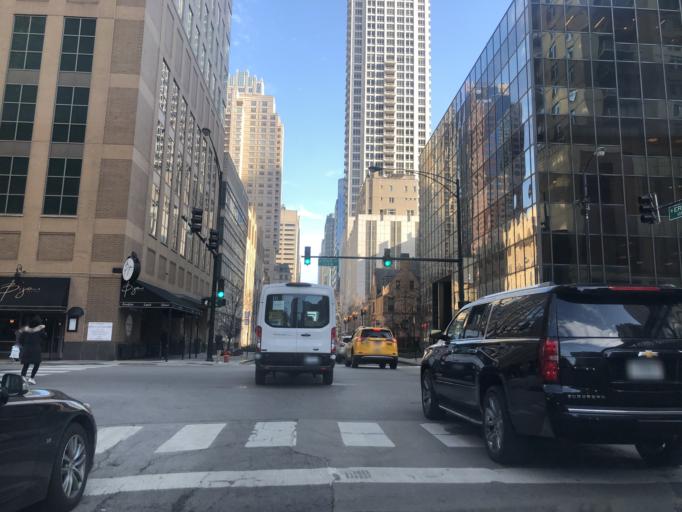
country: US
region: Illinois
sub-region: Cook County
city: Chicago
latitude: 41.8941
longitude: -87.6284
